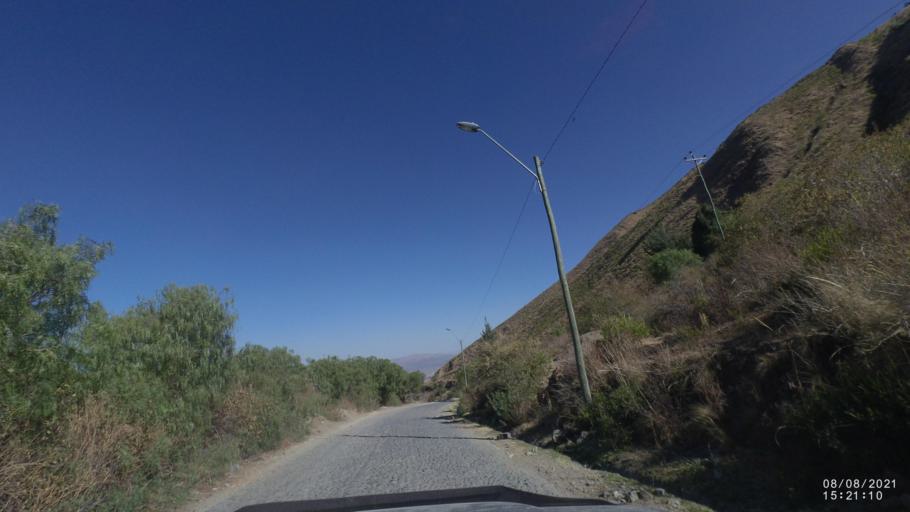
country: BO
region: Cochabamba
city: Cochabamba
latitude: -17.3005
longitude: -66.2956
